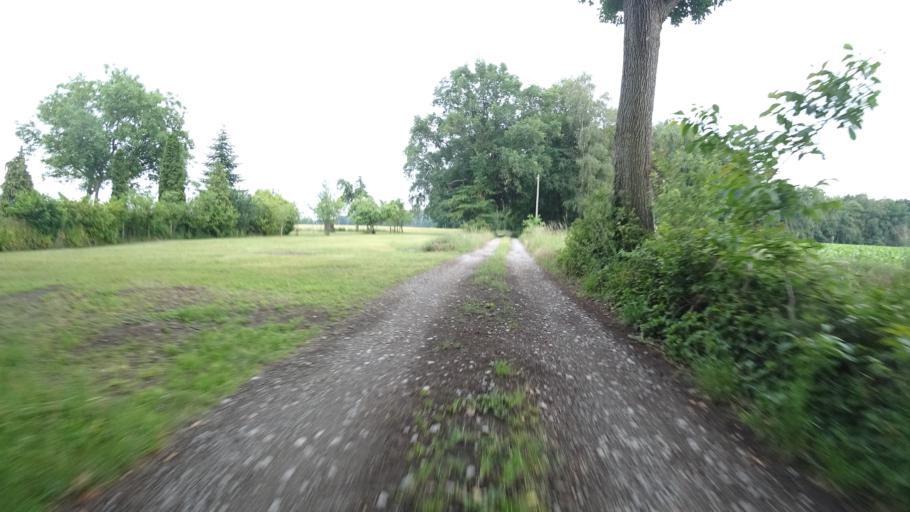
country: DE
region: North Rhine-Westphalia
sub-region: Regierungsbezirk Detmold
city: Guetersloh
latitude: 51.9479
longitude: 8.3282
